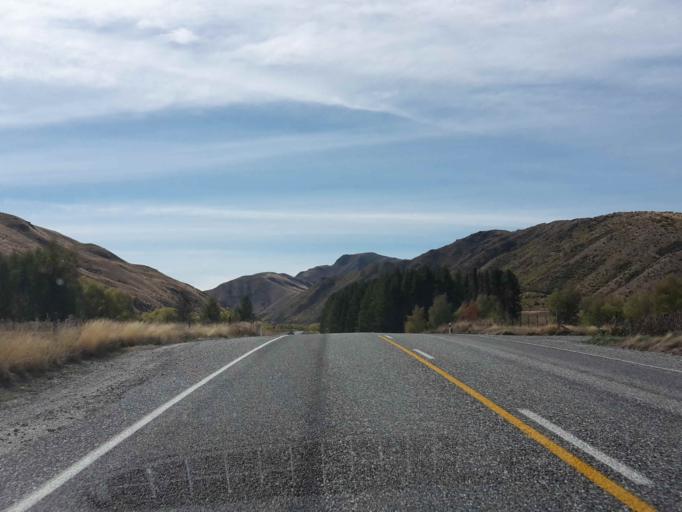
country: NZ
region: Otago
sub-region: Queenstown-Lakes District
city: Wanaka
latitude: -44.6390
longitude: 169.5084
